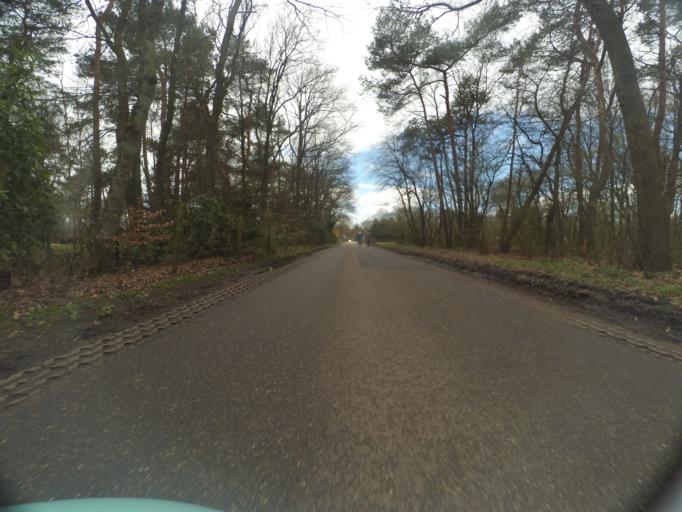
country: NL
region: Gelderland
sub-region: Gemeente Apeldoorn
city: Beekbergen
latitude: 52.1204
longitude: 5.9059
